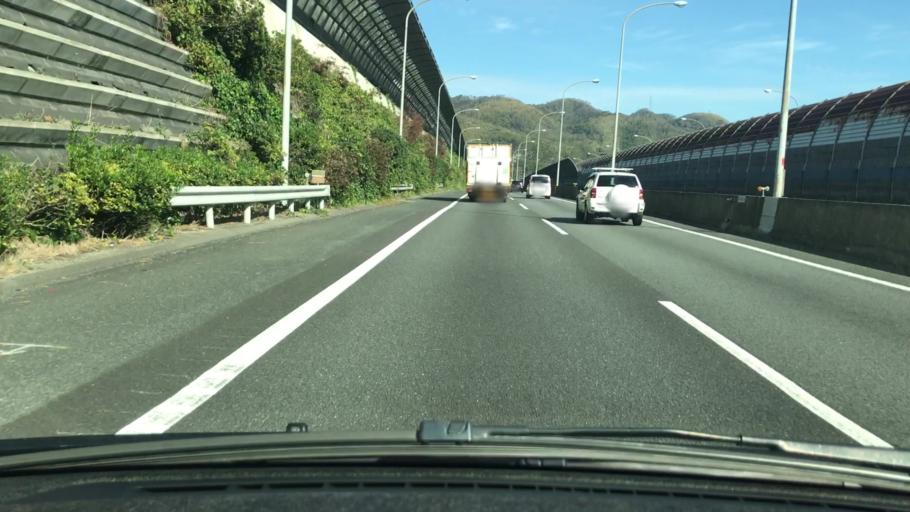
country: JP
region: Kyoto
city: Yawata
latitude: 34.8824
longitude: 135.6590
